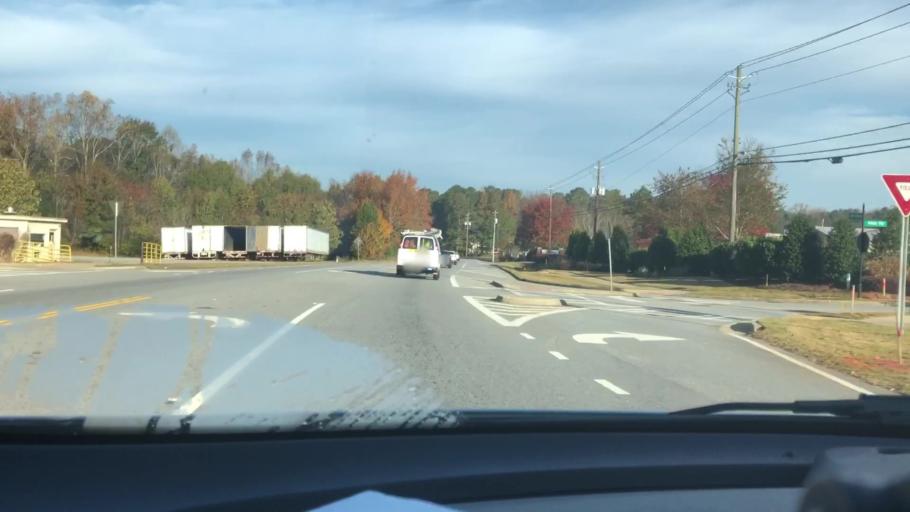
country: US
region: Georgia
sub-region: Gwinnett County
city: Duluth
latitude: 34.0225
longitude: -84.1631
